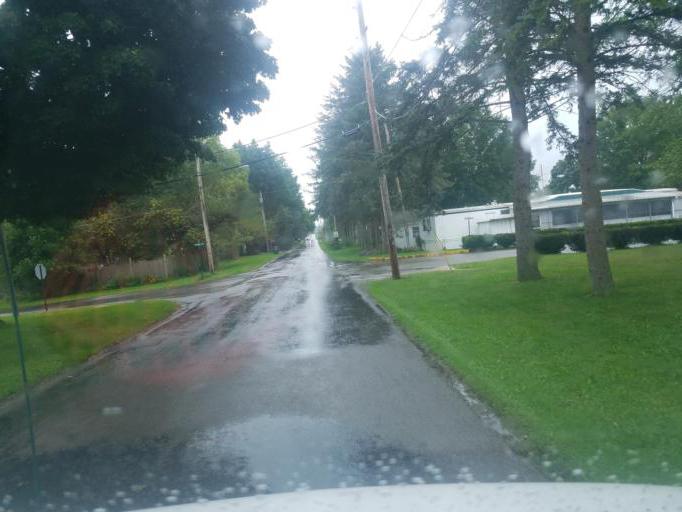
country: US
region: Ohio
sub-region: Wayne County
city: Creston
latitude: 40.9814
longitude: -81.9095
